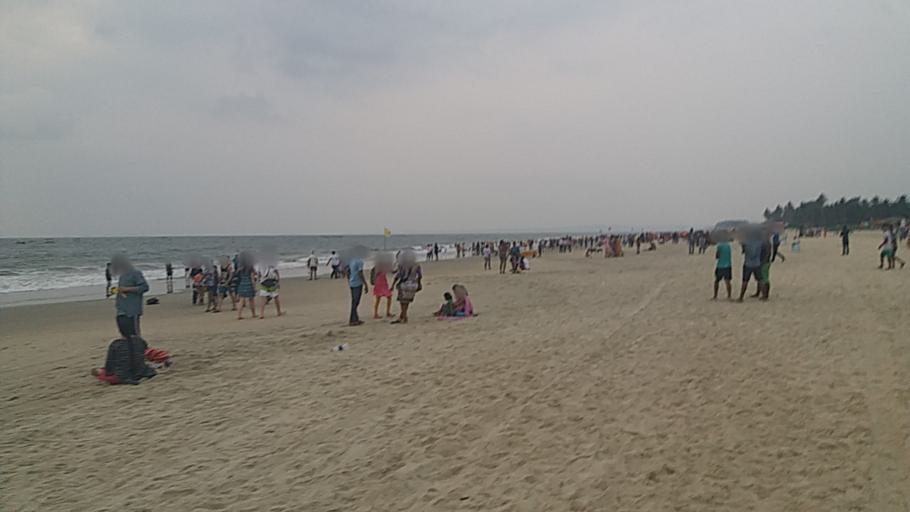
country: IN
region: Goa
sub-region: South Goa
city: Colva
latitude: 15.2746
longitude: 73.9136
